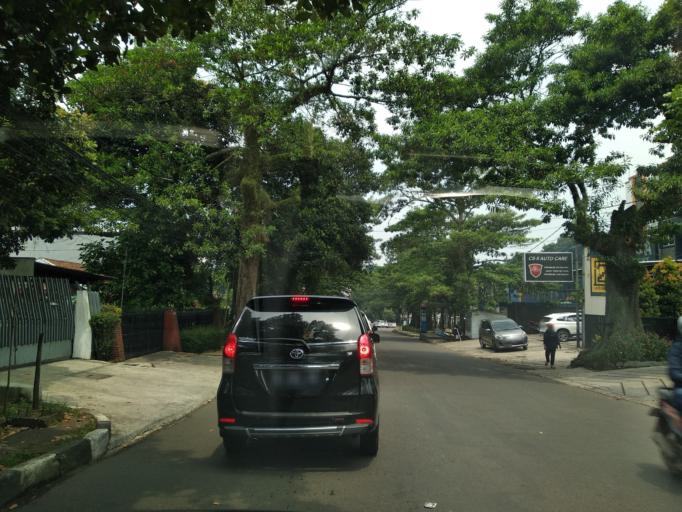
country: ID
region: West Java
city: Bandung
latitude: -6.8832
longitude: 107.5965
